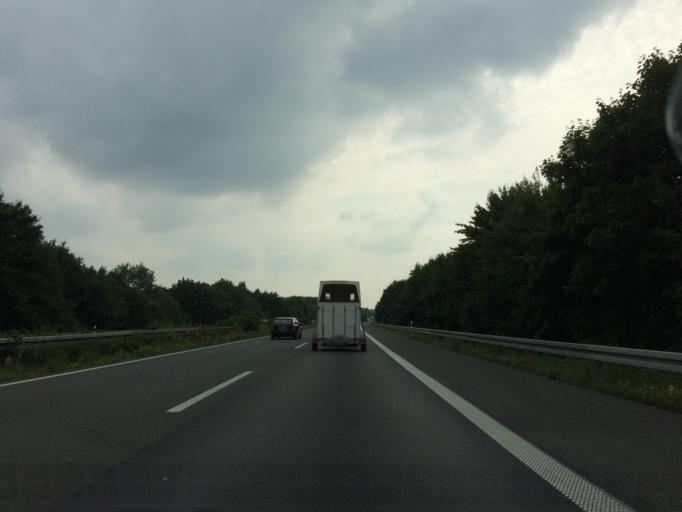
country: DE
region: North Rhine-Westphalia
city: Dorsten
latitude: 51.7339
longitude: 6.9522
